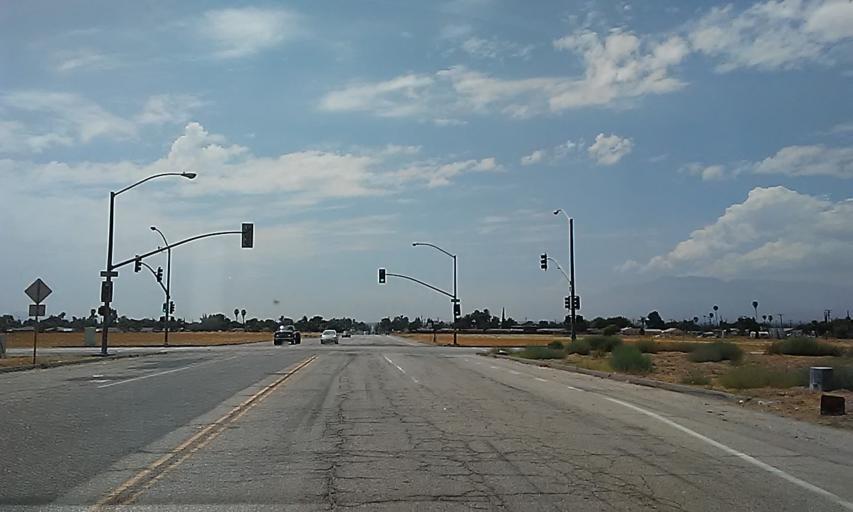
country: US
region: California
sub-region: San Bernardino County
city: Highland
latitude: 34.1083
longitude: -117.2431
